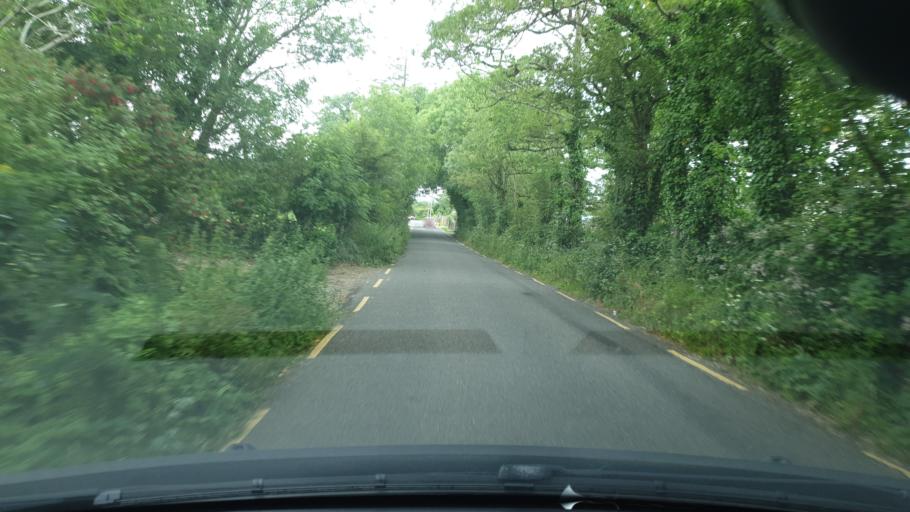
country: IE
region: Munster
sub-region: Ciarrai
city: Tralee
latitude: 52.2426
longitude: -9.6555
